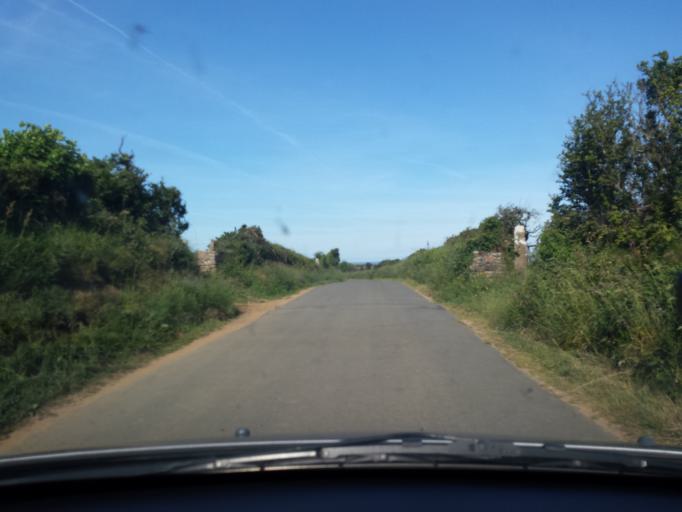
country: FR
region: Lower Normandy
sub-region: Departement de la Manche
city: Beaumont-Hague
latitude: 49.6760
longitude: -1.9239
